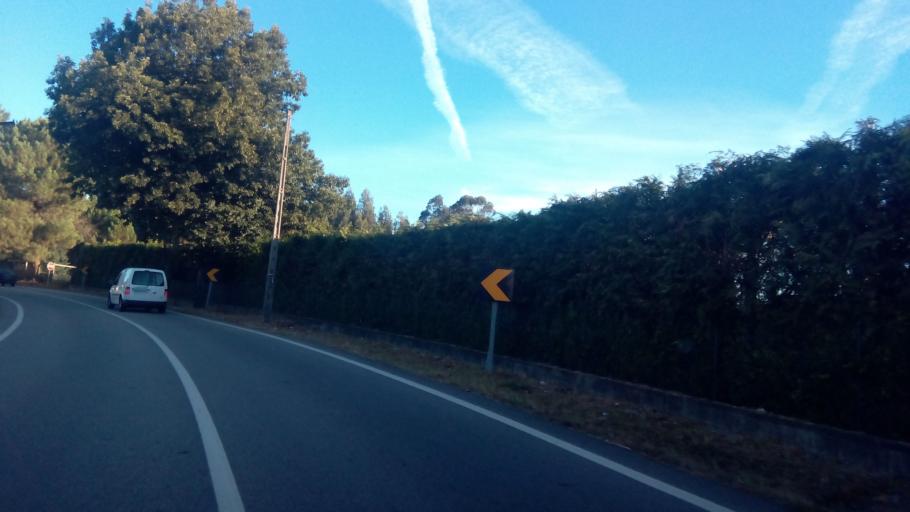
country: PT
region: Porto
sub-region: Paredes
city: Baltar
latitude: 41.1780
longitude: -8.3862
